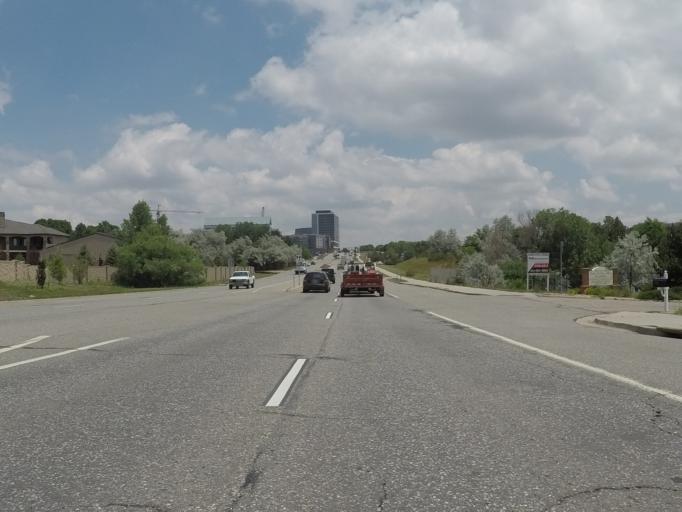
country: US
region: Colorado
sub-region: Arapahoe County
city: Greenwood Village
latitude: 39.6241
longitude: -104.9165
